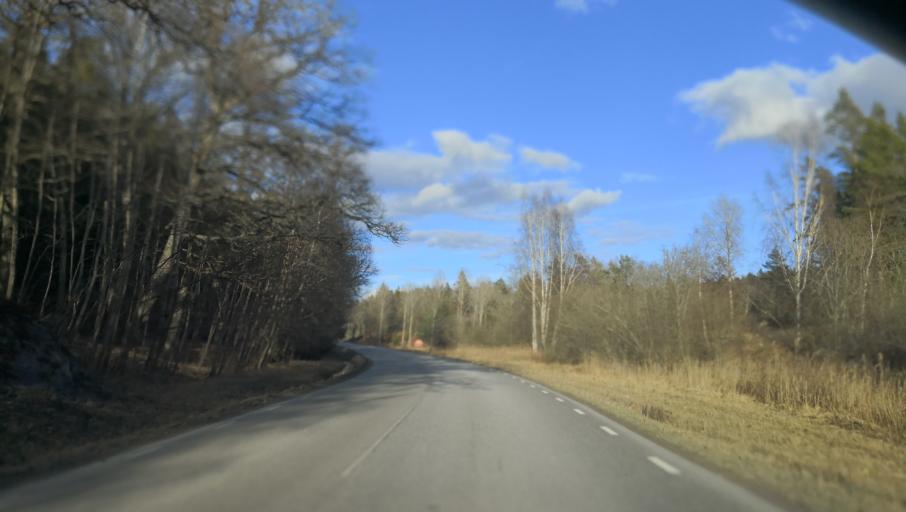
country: SE
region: Stockholm
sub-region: Varmdo Kommun
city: Gustavsberg
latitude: 59.3364
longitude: 18.3490
